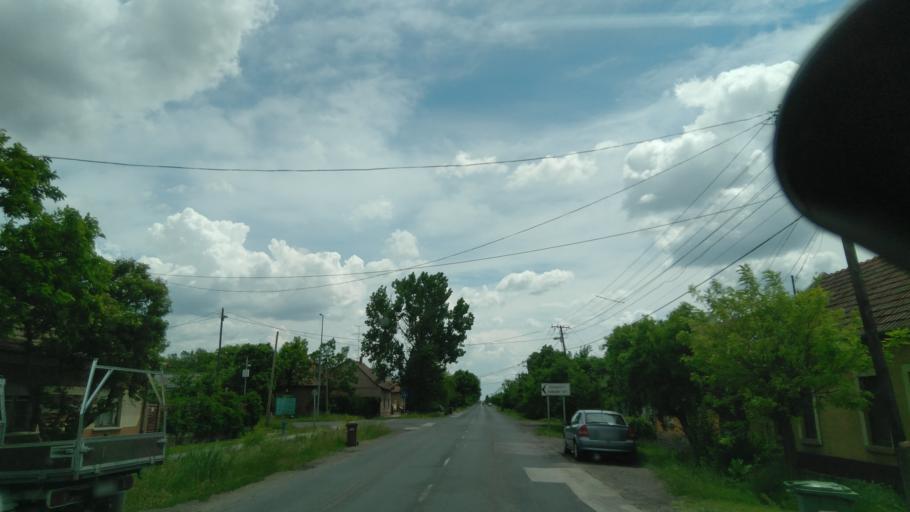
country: HU
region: Bekes
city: Oroshaza
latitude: 46.5450
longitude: 20.6757
